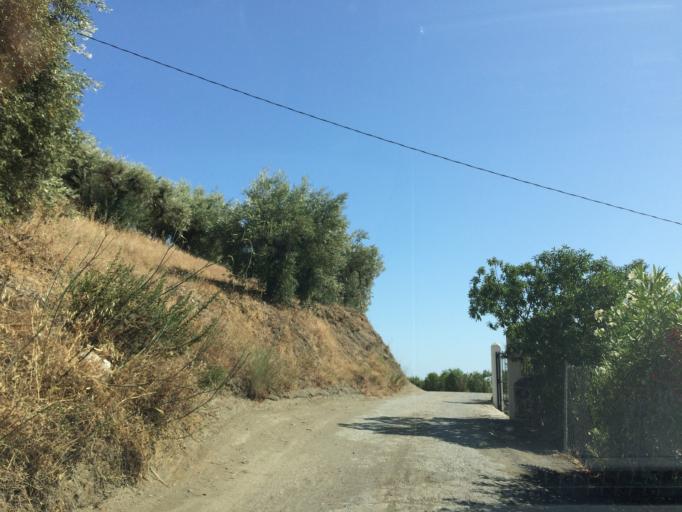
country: ES
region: Andalusia
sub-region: Provincia de Malaga
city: Frigiliana
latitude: 36.7983
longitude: -3.9105
